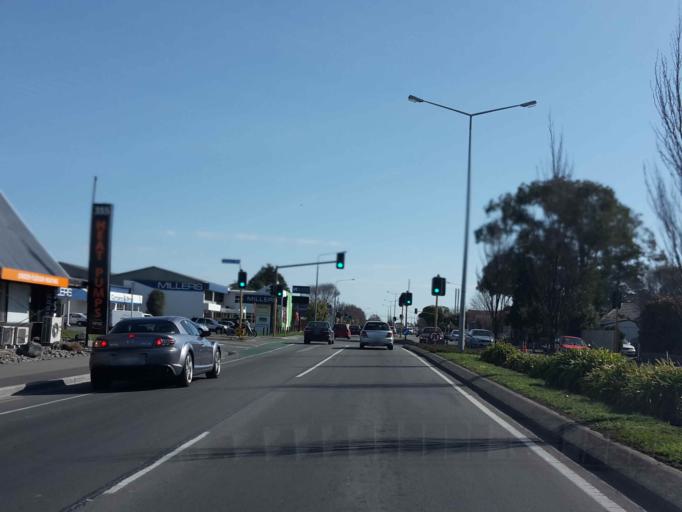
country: NZ
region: Canterbury
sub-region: Christchurch City
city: Christchurch
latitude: -43.5390
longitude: 172.5772
